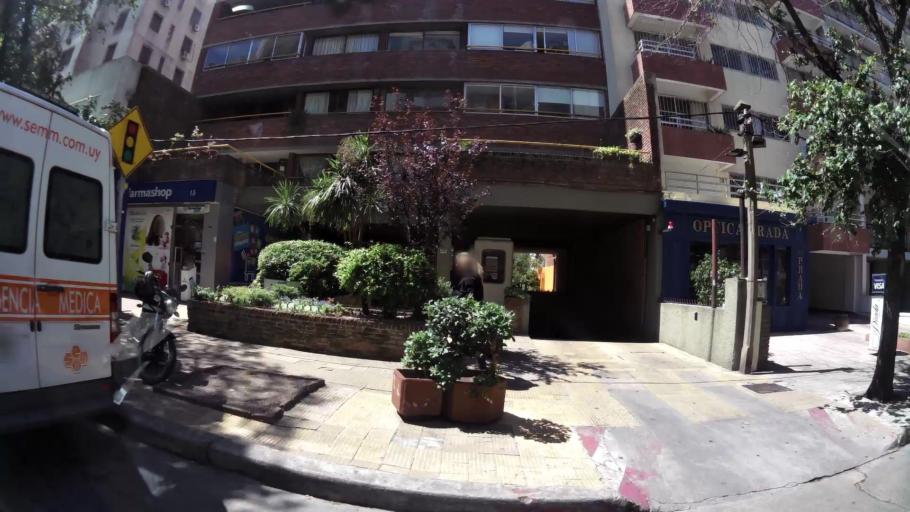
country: UY
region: Montevideo
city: Montevideo
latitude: -34.9190
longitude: -56.1551
